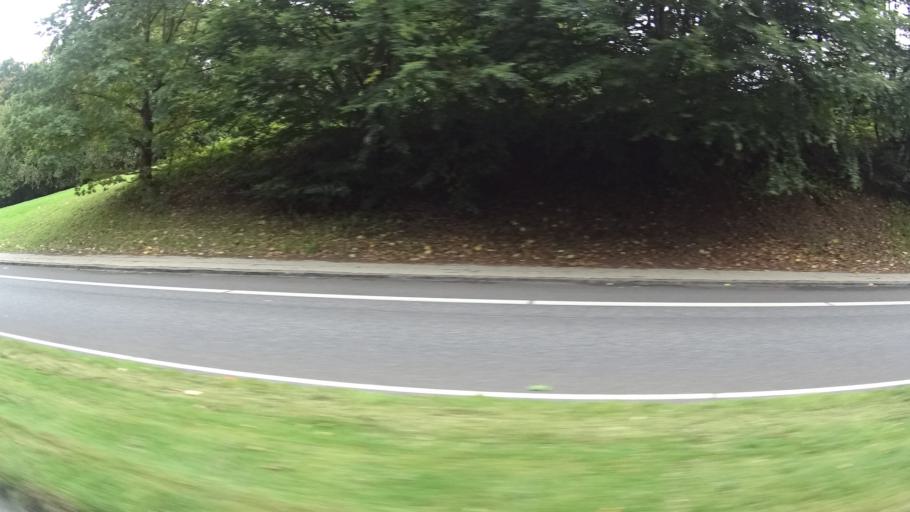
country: DK
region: South Denmark
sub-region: Vejle Kommune
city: Vejle
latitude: 55.6901
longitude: 9.5228
